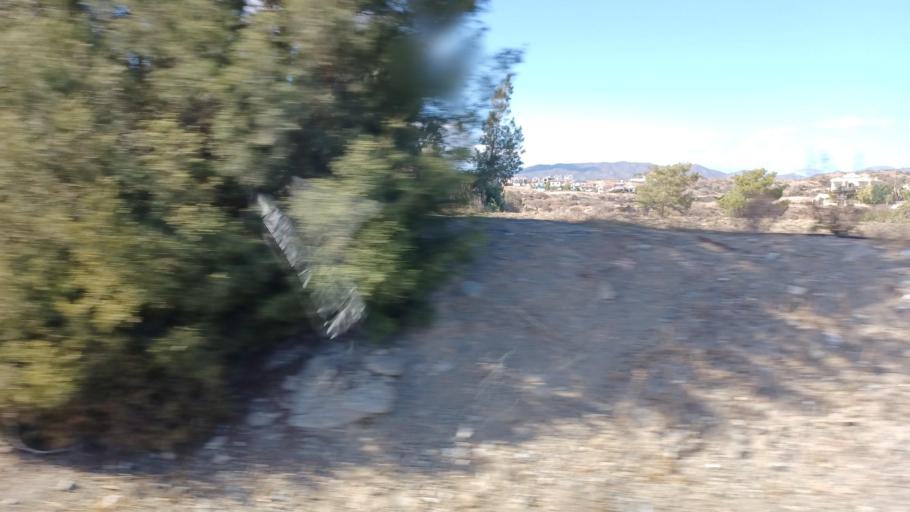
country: CY
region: Limassol
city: Pyrgos
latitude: 34.7401
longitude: 33.2107
